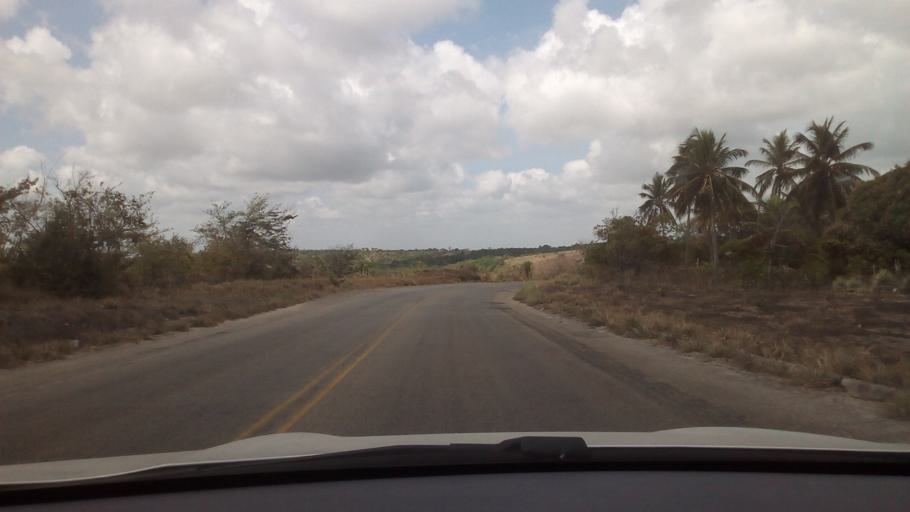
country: BR
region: Paraiba
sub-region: Conde
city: Conde
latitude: -7.2533
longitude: -34.8155
